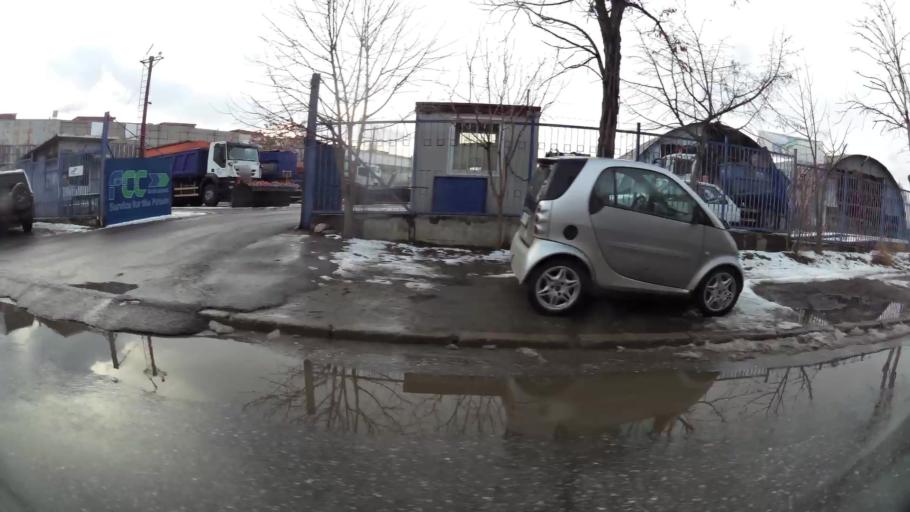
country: BG
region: Sofia-Capital
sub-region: Stolichna Obshtina
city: Sofia
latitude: 42.7248
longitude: 23.3301
